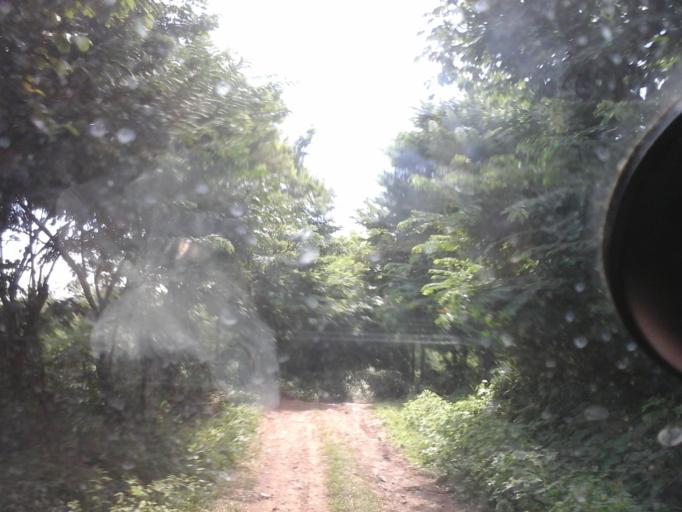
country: CO
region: Cesar
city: San Diego
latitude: 10.2733
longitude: -73.0937
